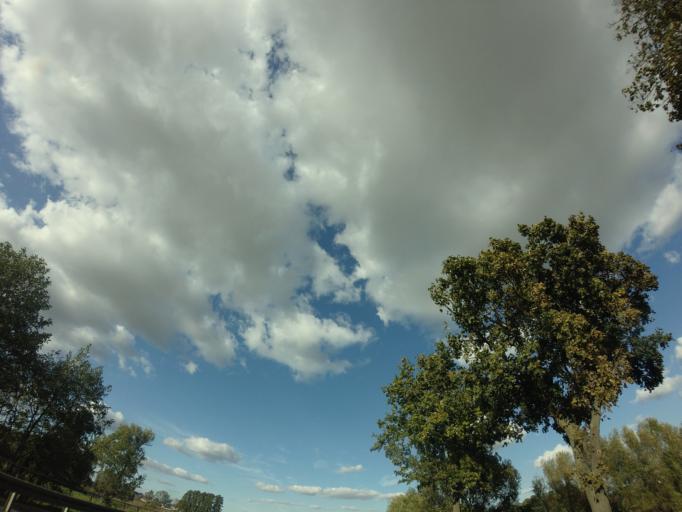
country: PL
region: Greater Poland Voivodeship
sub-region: Powiat koscianski
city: Smigiel
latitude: 52.0301
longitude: 16.5369
